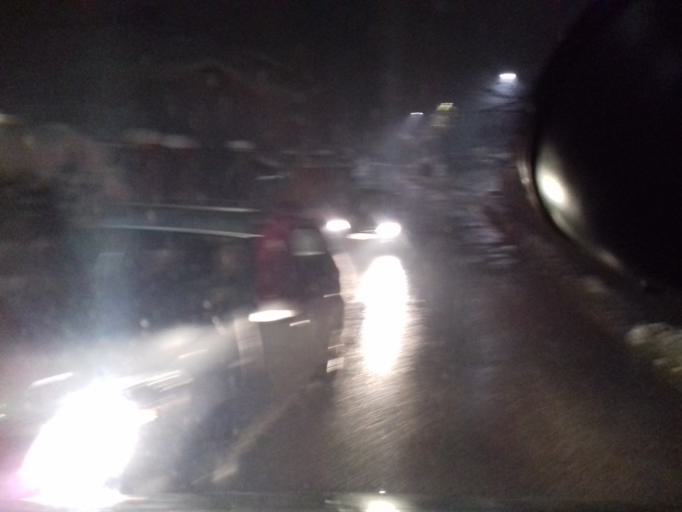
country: BA
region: Federation of Bosnia and Herzegovina
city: Kobilja Glava
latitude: 43.8667
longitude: 18.4210
